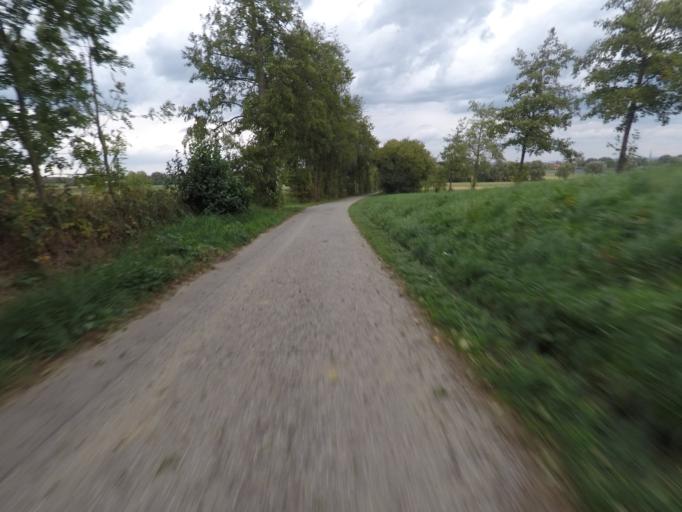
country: DE
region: Baden-Wuerttemberg
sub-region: Regierungsbezirk Stuttgart
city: Leinfelden-Echterdingen
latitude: 48.6668
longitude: 9.1870
